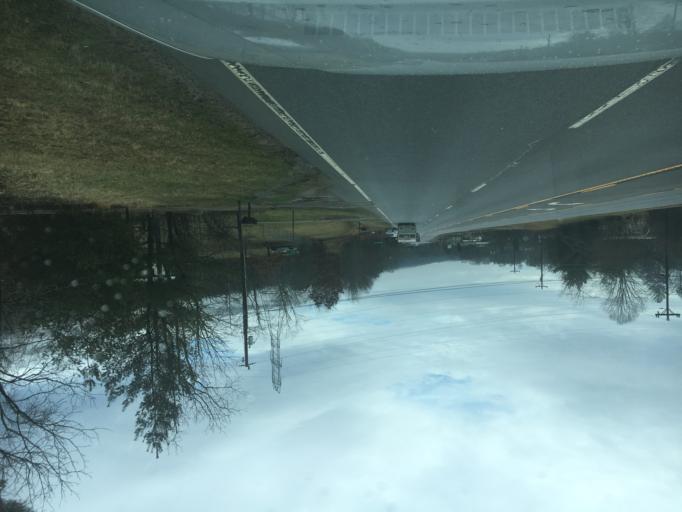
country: US
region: North Carolina
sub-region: Henderson County
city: Etowah
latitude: 35.3483
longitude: -82.6160
